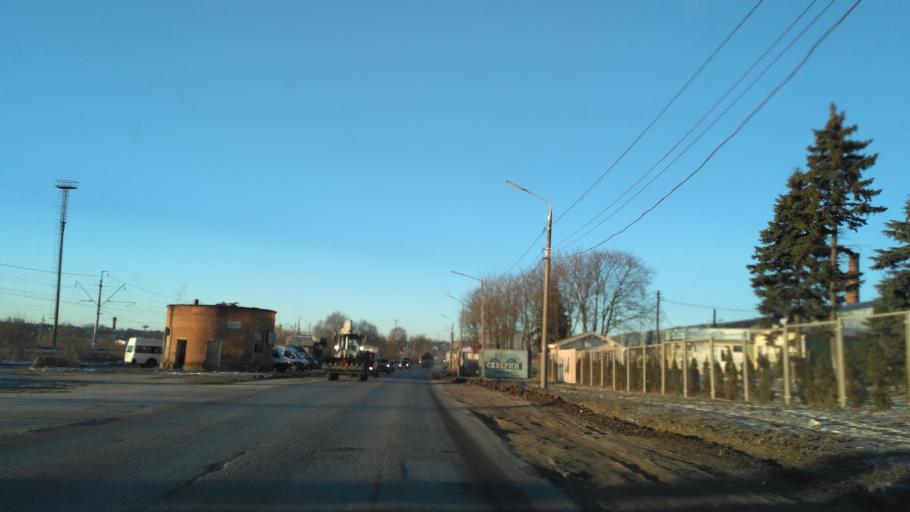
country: RU
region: Tula
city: Gorelki
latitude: 54.2271
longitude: 37.5790
